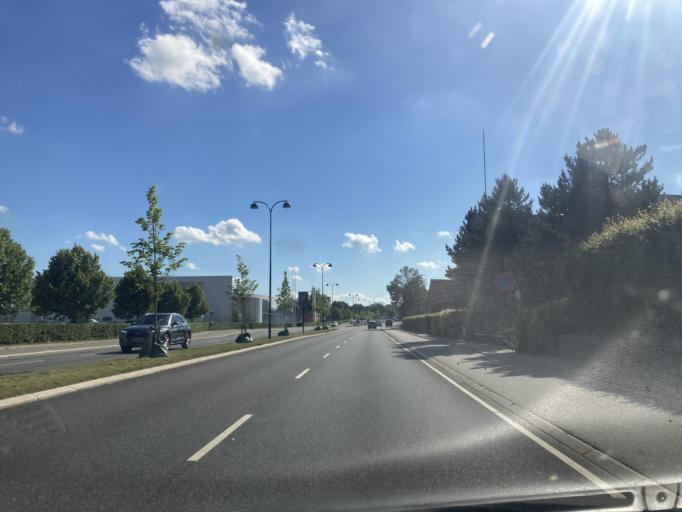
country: DK
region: Capital Region
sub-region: Rudersdal Kommune
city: Birkerod
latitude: 55.8405
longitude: 12.4358
